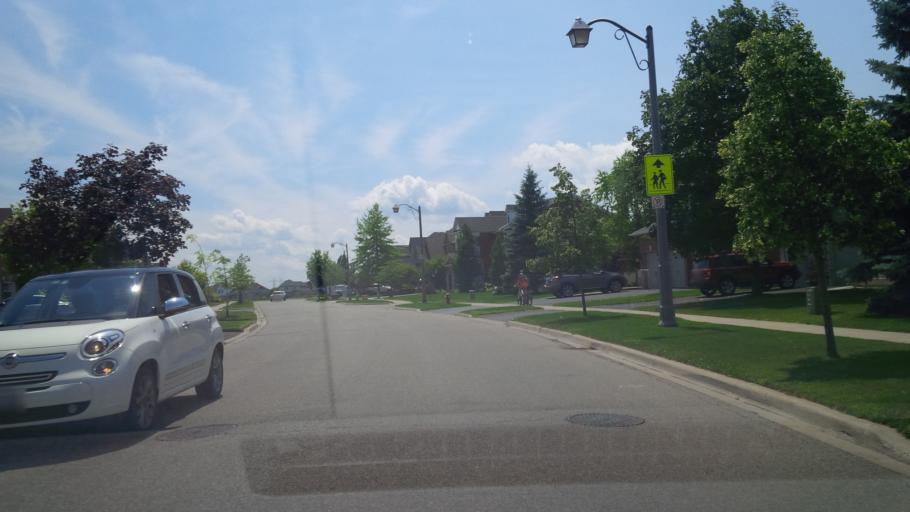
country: CA
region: Ontario
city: Burlington
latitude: 43.4003
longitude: -79.8082
